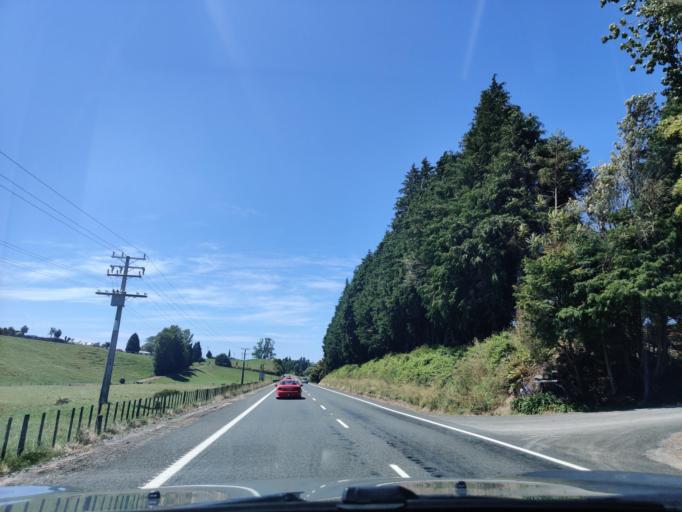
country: NZ
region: Waikato
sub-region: Otorohanga District
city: Otorohanga
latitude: -38.2110
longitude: 175.1979
